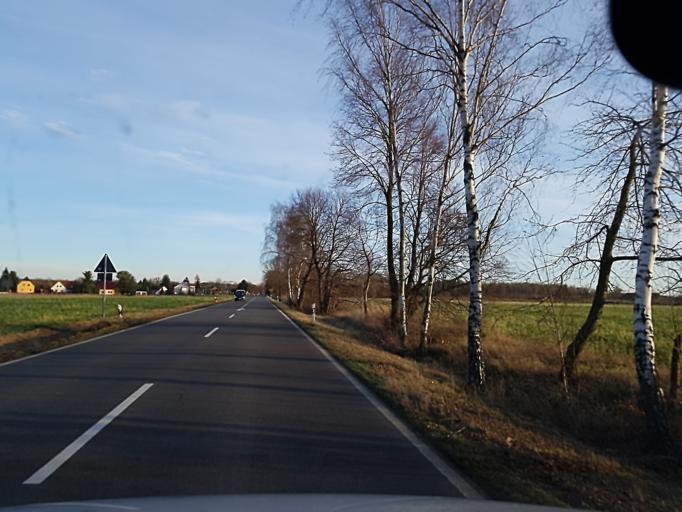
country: DE
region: Brandenburg
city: Finsterwalde
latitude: 51.6159
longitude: 13.7514
